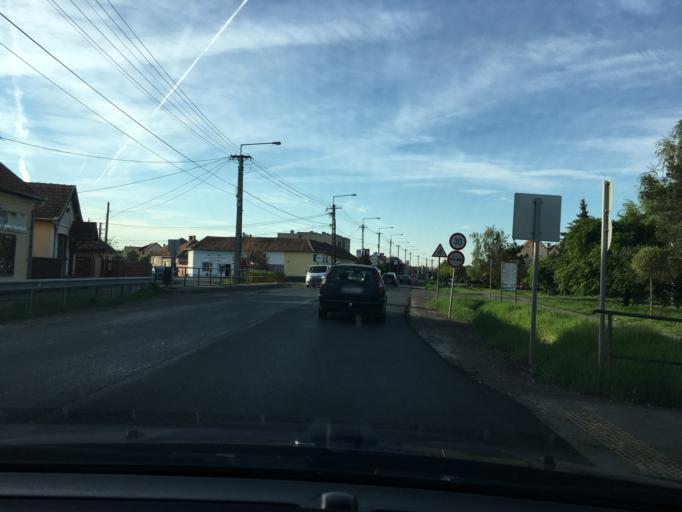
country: HU
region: Hajdu-Bihar
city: Berettyoujfalu
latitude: 47.2280
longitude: 21.5332
